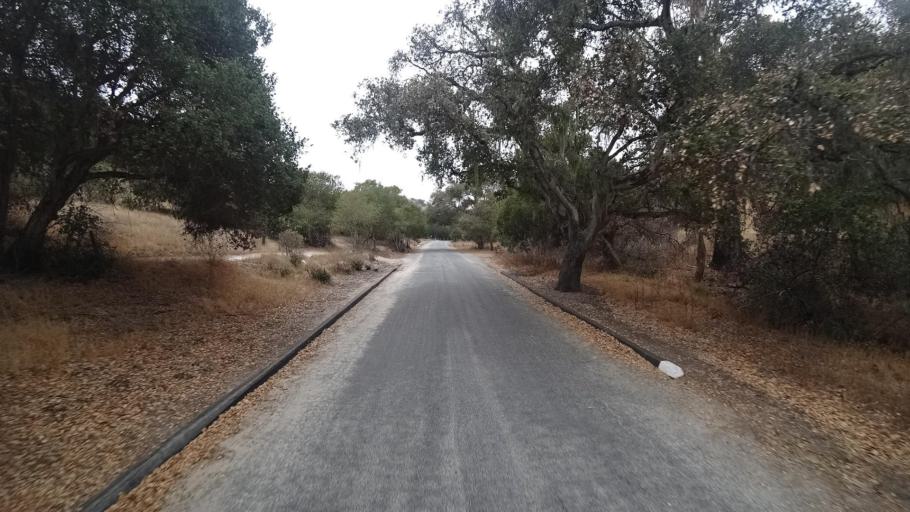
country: US
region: California
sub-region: Monterey County
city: Salinas
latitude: 36.5914
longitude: -121.6902
